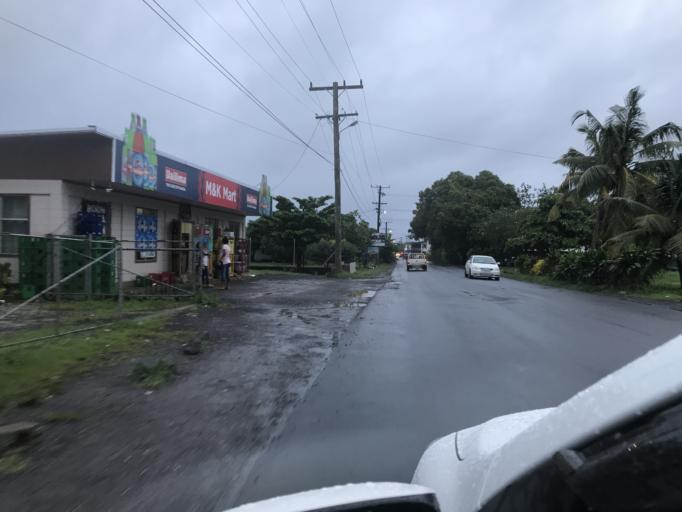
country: WS
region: Tuamasaga
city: Apia
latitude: -13.8356
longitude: -171.7554
